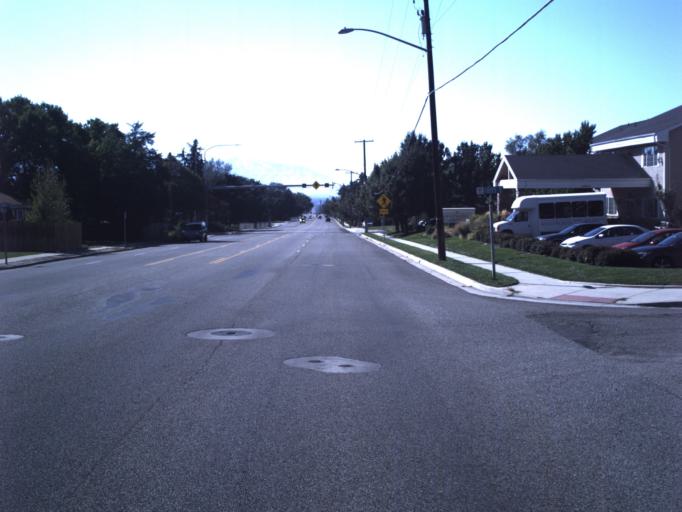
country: US
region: Utah
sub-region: Salt Lake County
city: Willard
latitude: 40.7000
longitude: -111.8373
